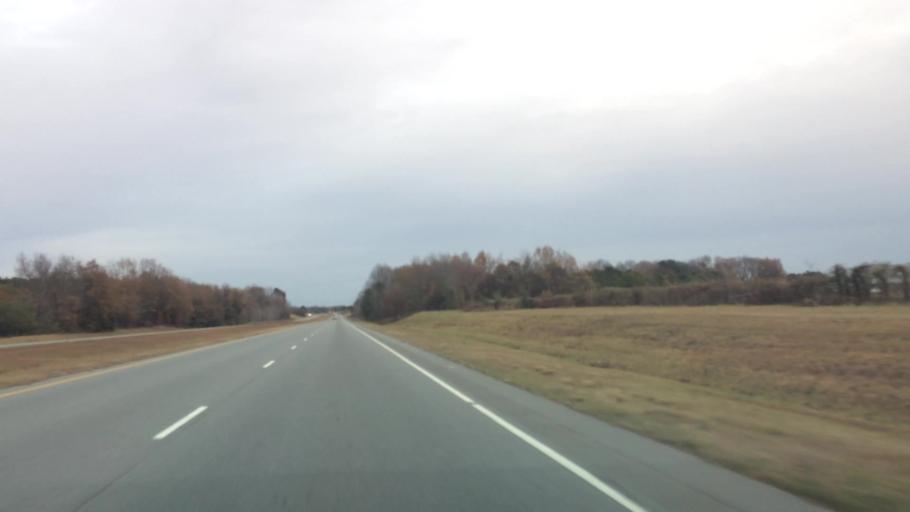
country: US
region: North Carolina
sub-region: Wayne County
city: Mount Olive
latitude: 35.1254
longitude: -78.1655
